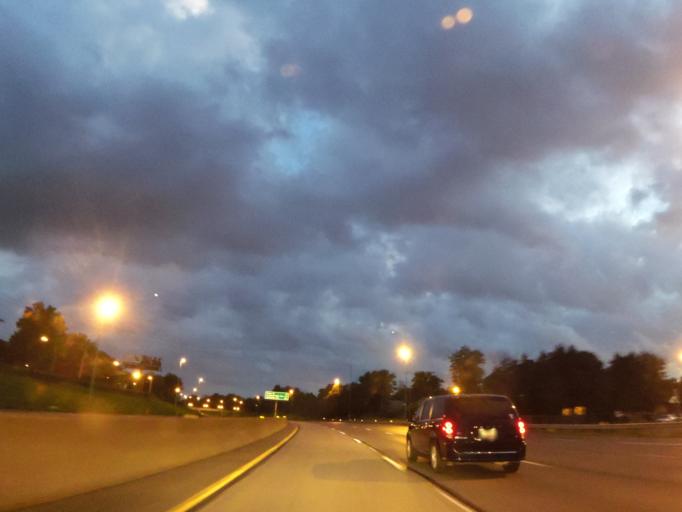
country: US
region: Illinois
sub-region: Saint Clair County
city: Cahokia
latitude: 38.5729
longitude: -90.2362
